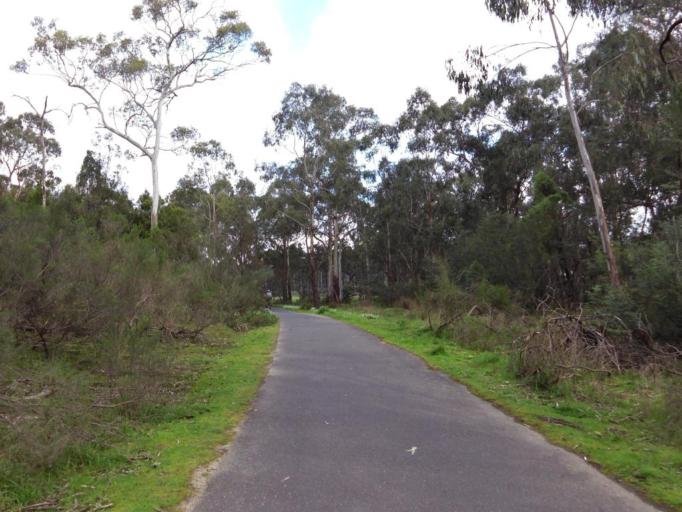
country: AU
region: Victoria
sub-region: Nillumbik
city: Eltham
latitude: -37.7498
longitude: 145.1741
